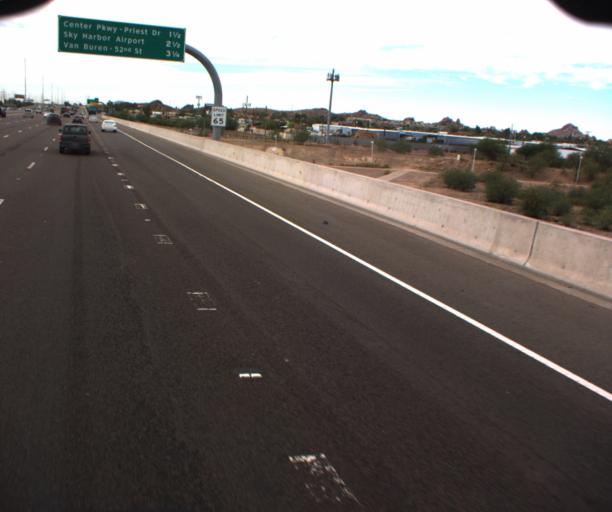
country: US
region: Arizona
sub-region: Maricopa County
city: Tempe
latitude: 33.4363
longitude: -111.9168
